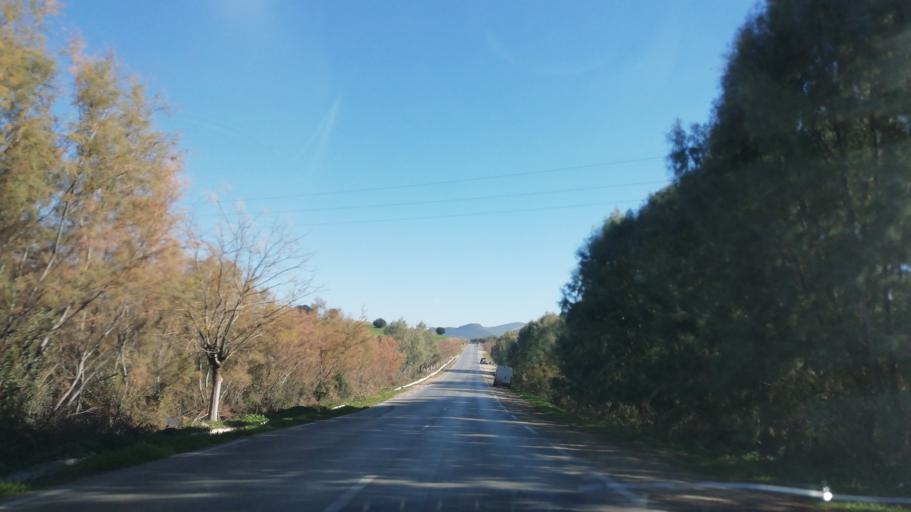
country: DZ
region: Tlemcen
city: Beni Mester
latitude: 34.8246
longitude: -1.5509
